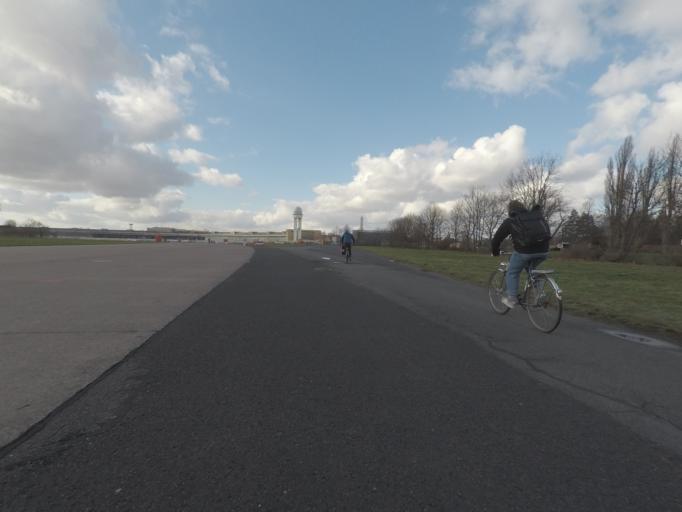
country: DE
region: Berlin
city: Tempelhof Bezirk
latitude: 52.4792
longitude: 13.4077
